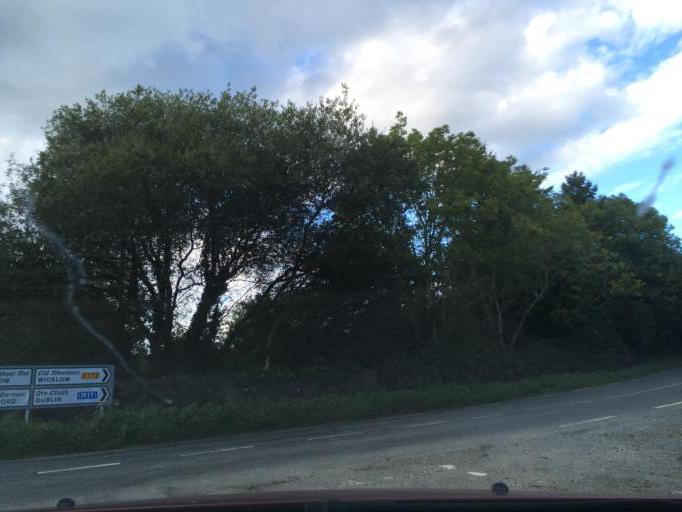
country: IE
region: Leinster
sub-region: Wicklow
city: Wicklow
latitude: 52.9568
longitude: -6.0705
